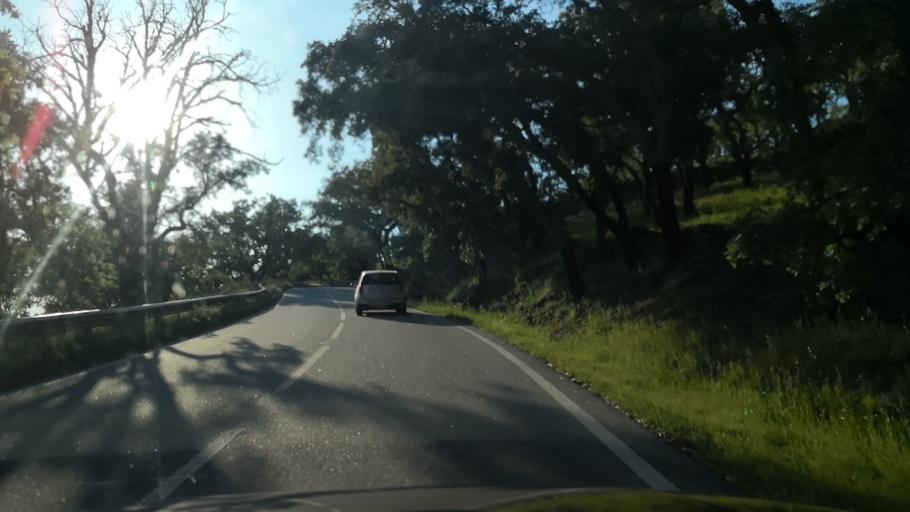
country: PT
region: Portalegre
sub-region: Portalegre
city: Portalegre
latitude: 39.3318
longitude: -7.4248
